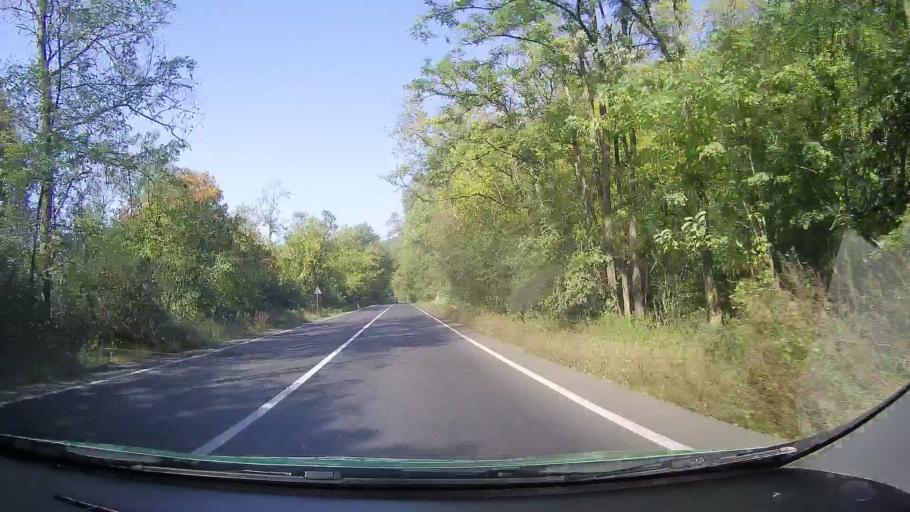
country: RO
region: Arad
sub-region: Comuna Savarsin
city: Savarsin
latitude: 46.0083
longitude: 22.2728
